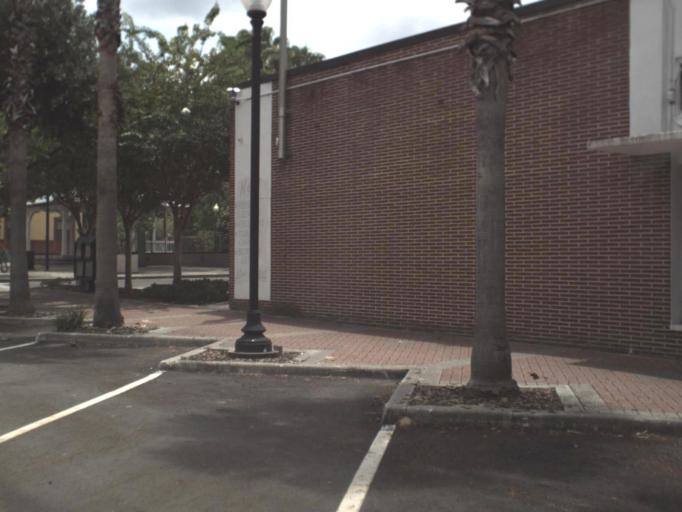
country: US
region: Florida
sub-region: Pasco County
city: Zephyrhills
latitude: 28.2341
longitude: -82.1802
